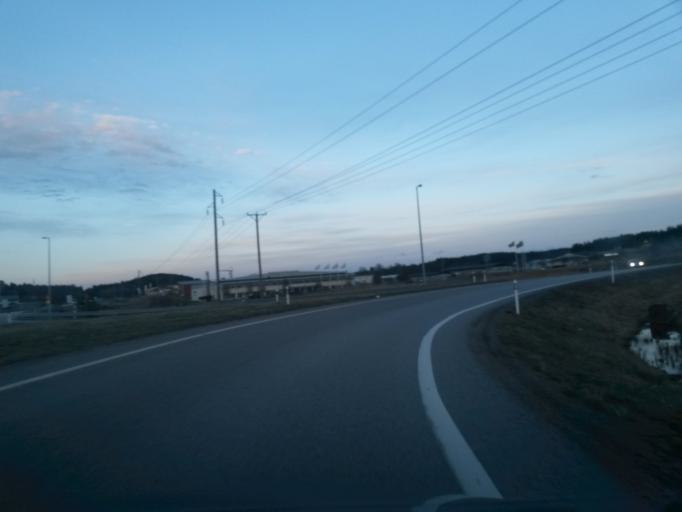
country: SE
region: Vaestra Goetaland
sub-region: Vargarda Kommun
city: Vargarda
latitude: 58.0414
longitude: 12.7970
